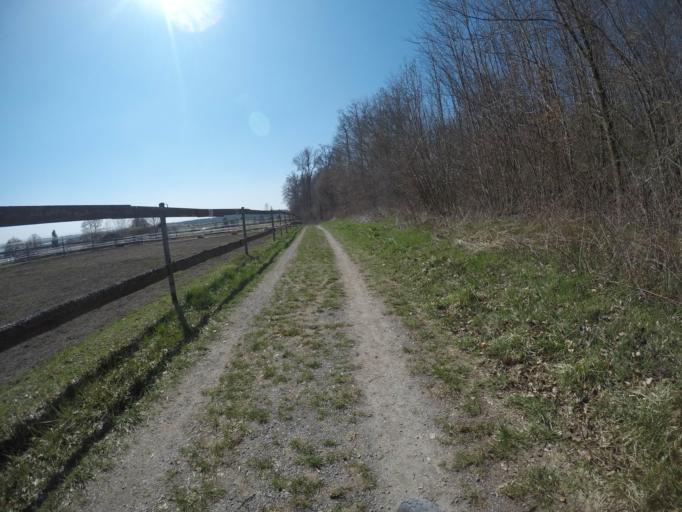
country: DE
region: Baden-Wuerttemberg
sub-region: Regierungsbezirk Stuttgart
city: Herrenberg
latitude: 48.5928
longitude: 8.8264
